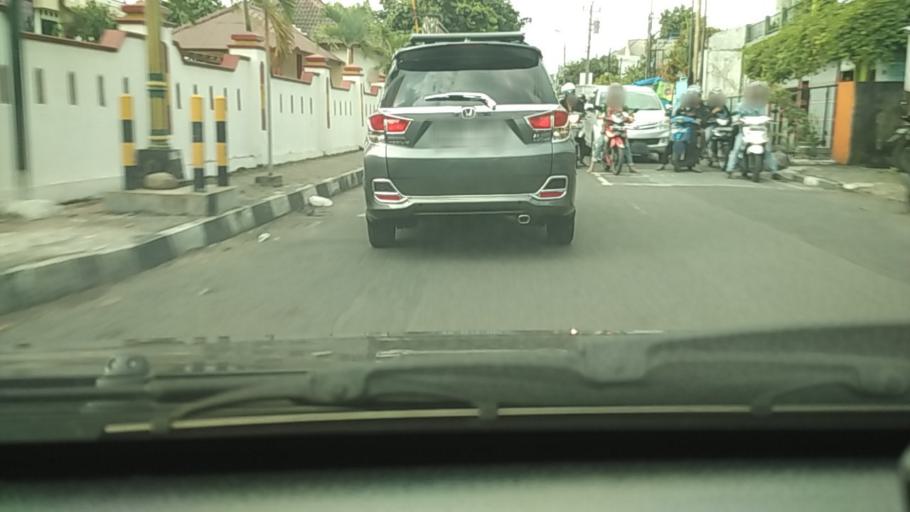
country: ID
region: Daerah Istimewa Yogyakarta
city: Yogyakarta
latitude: -7.7914
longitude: 110.3862
